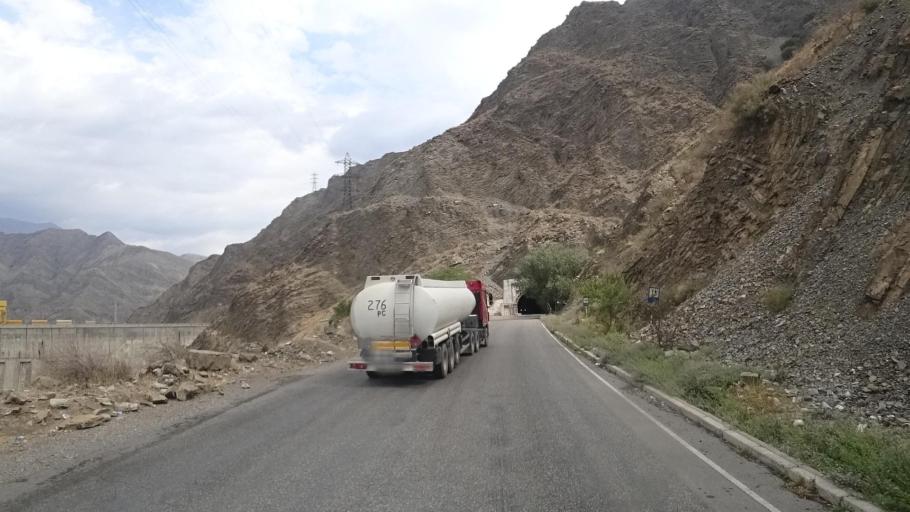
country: KG
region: Jalal-Abad
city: Tash-Kumyr
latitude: 41.4945
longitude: 72.3635
